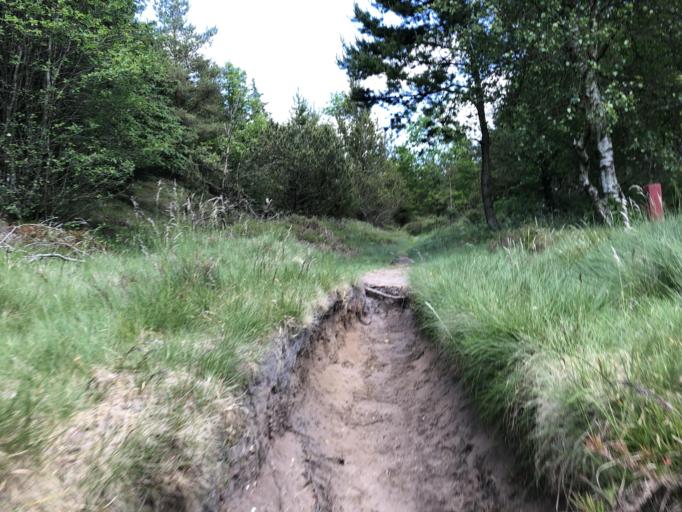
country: DK
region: Central Jutland
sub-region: Lemvig Kommune
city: Lemvig
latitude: 56.4886
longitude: 8.3738
